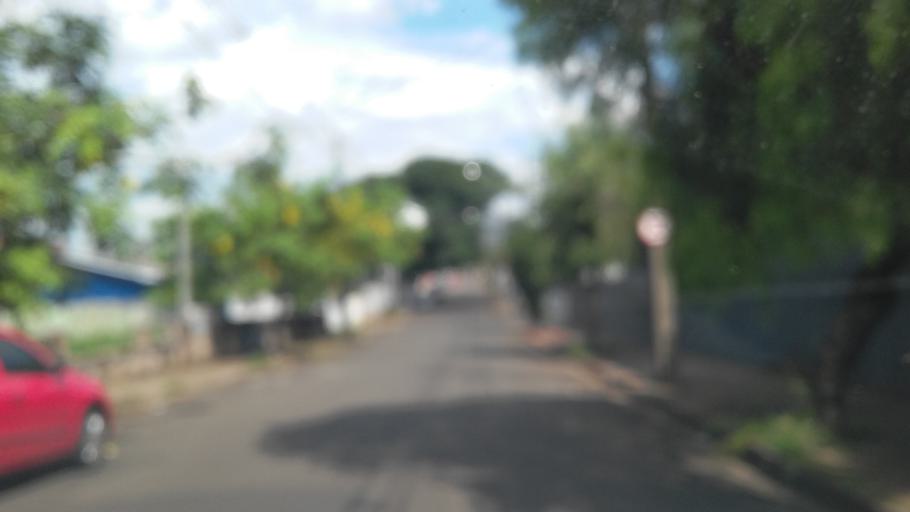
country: BR
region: Parana
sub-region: Londrina
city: Londrina
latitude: -23.3024
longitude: -51.1702
